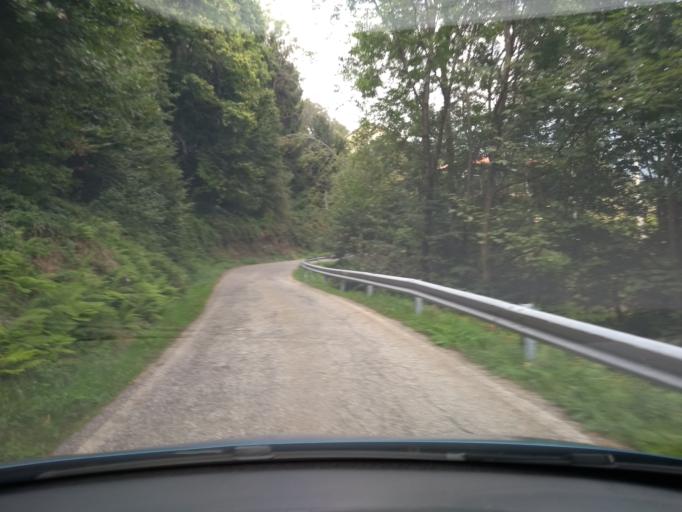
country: IT
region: Piedmont
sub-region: Provincia di Torino
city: Corio
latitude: 45.3272
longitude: 7.5172
